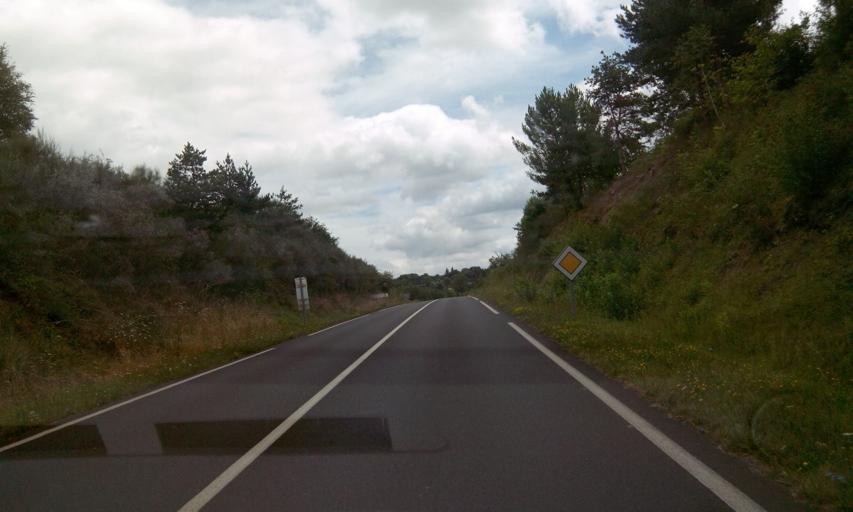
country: FR
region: Limousin
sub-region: Departement de la Correze
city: Cosnac
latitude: 45.1013
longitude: 1.5758
